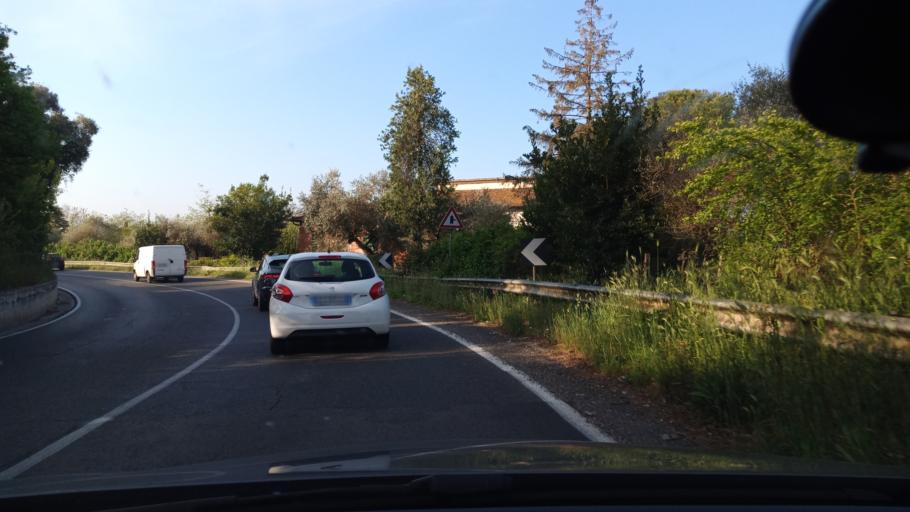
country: IT
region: Latium
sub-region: Citta metropolitana di Roma Capitale
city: Fiano Romano
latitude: 42.1717
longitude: 12.6354
